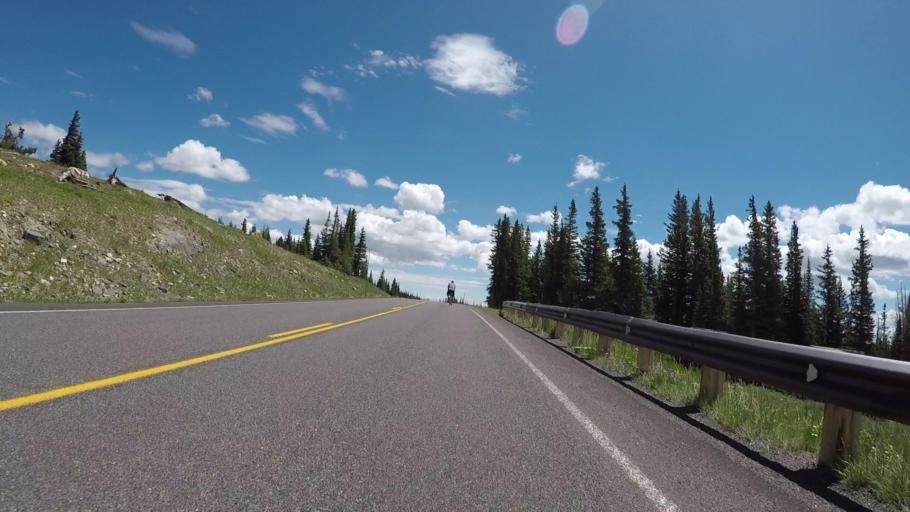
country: US
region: Wyoming
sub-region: Carbon County
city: Saratoga
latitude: 41.3511
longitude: -106.2748
